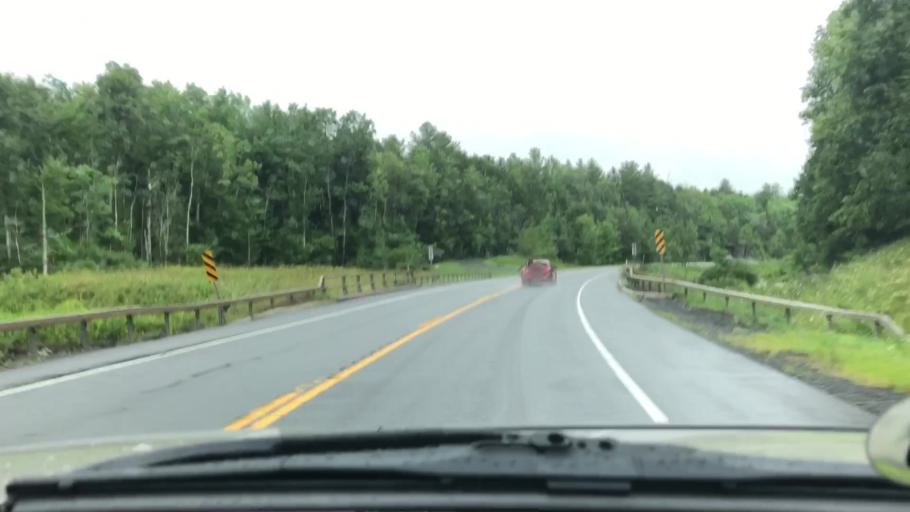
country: US
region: New York
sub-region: Greene County
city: Cairo
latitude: 42.3076
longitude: -74.1930
